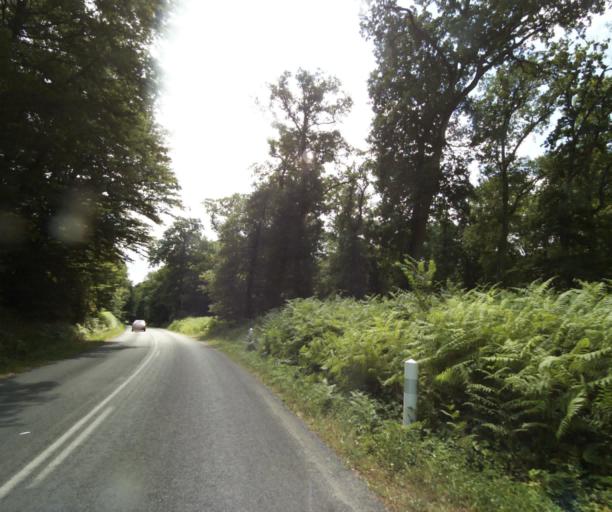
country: FR
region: Ile-de-France
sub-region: Departement de Seine-et-Marne
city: Bois-le-Roi
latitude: 48.4637
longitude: 2.7132
